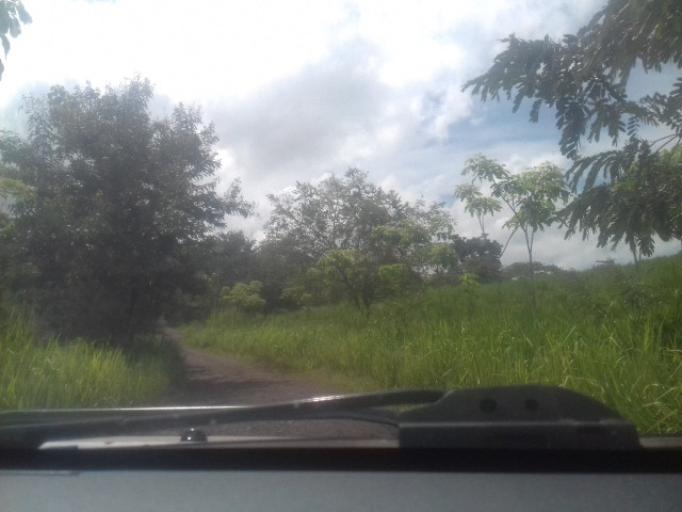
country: NI
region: Jinotega
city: San Jose de Bocay
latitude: 13.5037
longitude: -85.2370
